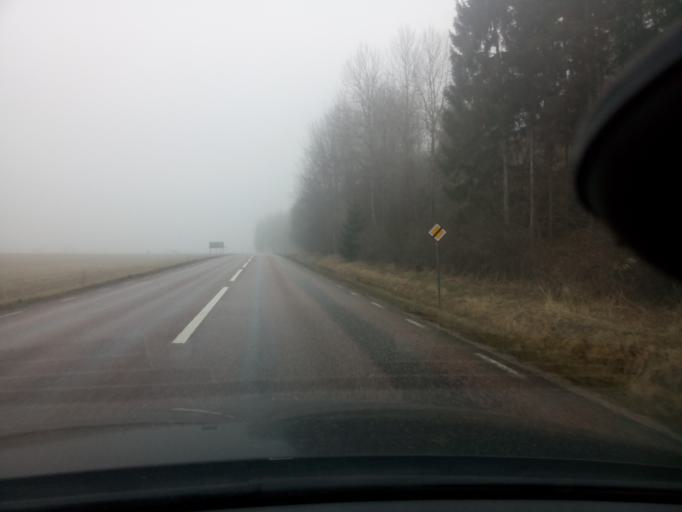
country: SE
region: Soedermanland
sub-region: Nykopings Kommun
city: Nykoping
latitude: 58.8148
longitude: 17.0802
